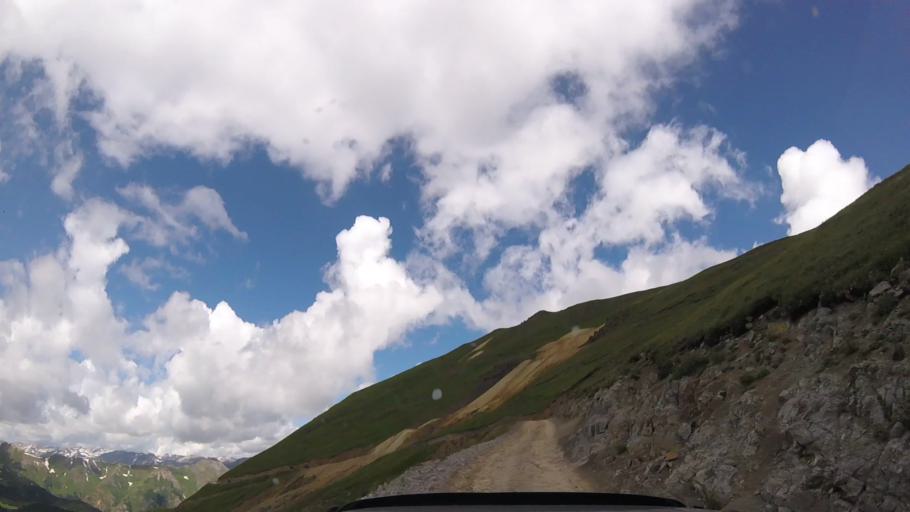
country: US
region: Colorado
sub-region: Ouray County
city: Ouray
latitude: 37.9659
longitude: -107.5797
